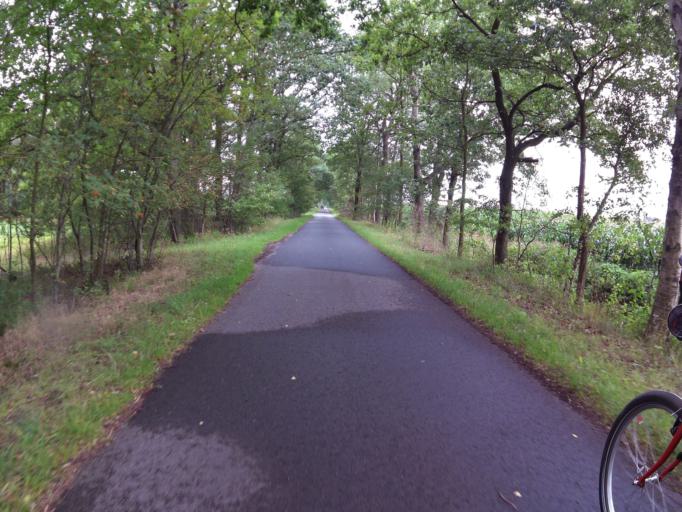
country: DE
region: Lower Saxony
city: Scheessel
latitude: 53.1457
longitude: 9.4456
